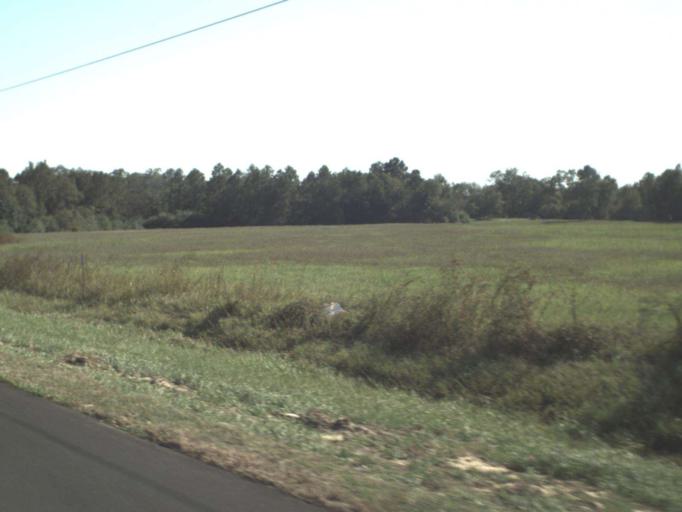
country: US
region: Florida
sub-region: Walton County
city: DeFuniak Springs
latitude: 30.8093
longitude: -86.2004
